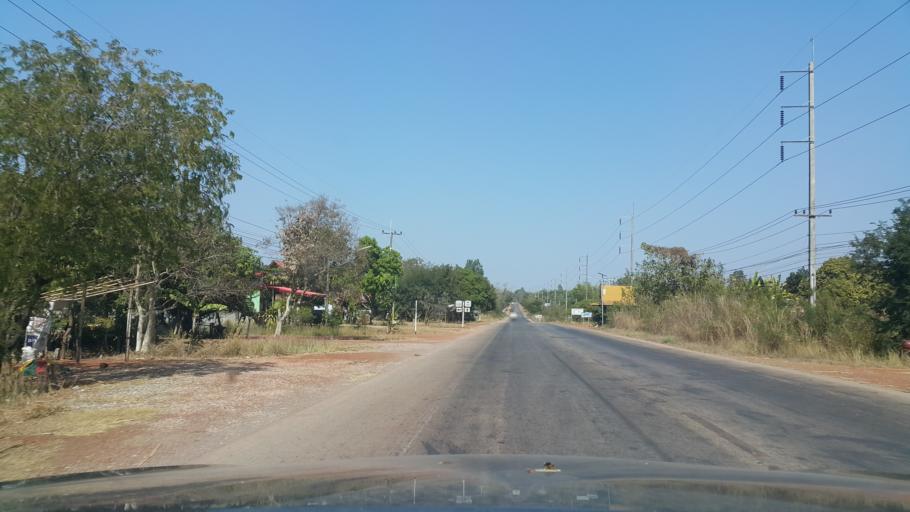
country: TH
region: Changwat Udon Thani
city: Ban Dung
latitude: 17.5951
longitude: 103.2460
